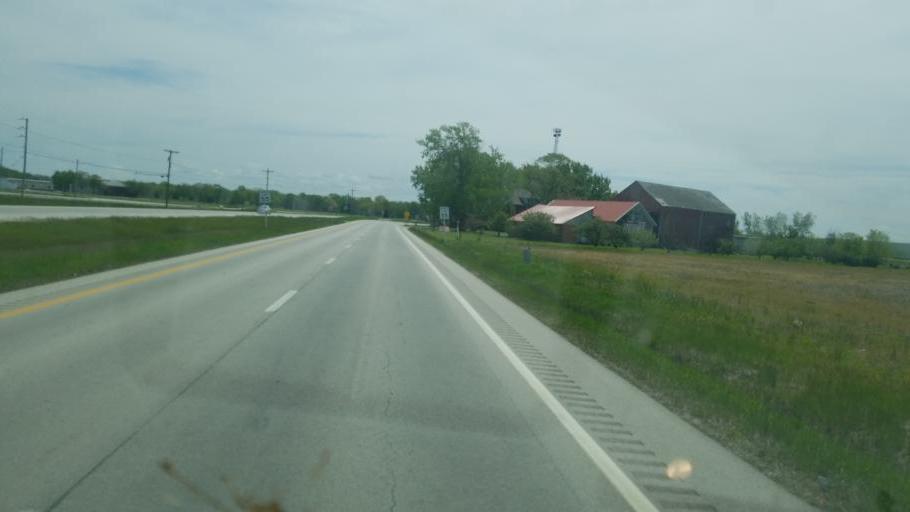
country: US
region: Ohio
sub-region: Ottawa County
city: Port Clinton
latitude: 41.5421
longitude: -83.0415
